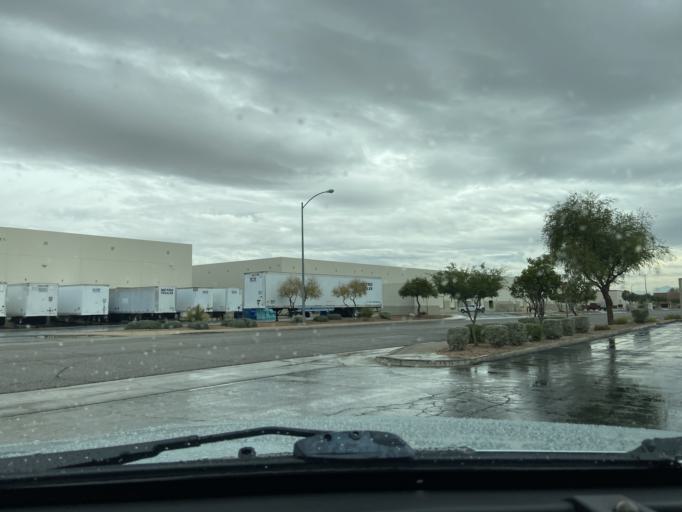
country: US
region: Nevada
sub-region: Clark County
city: Sunrise Manor
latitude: 36.2347
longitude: -115.1006
